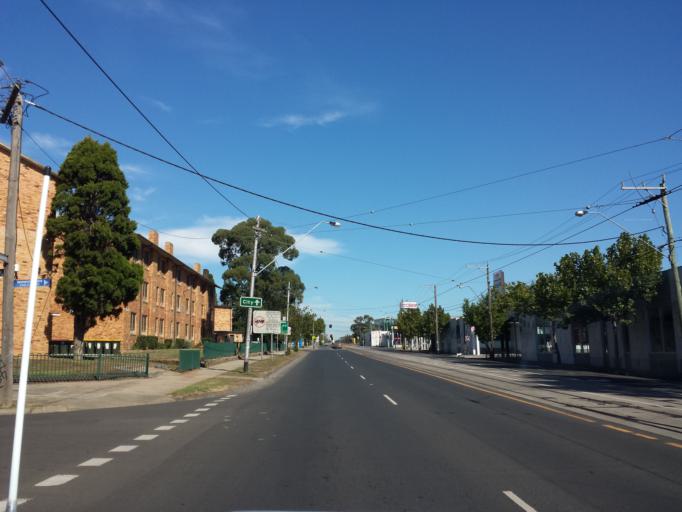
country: AU
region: Victoria
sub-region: Melbourne
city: Ascot Vale
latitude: -37.7810
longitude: 144.9152
